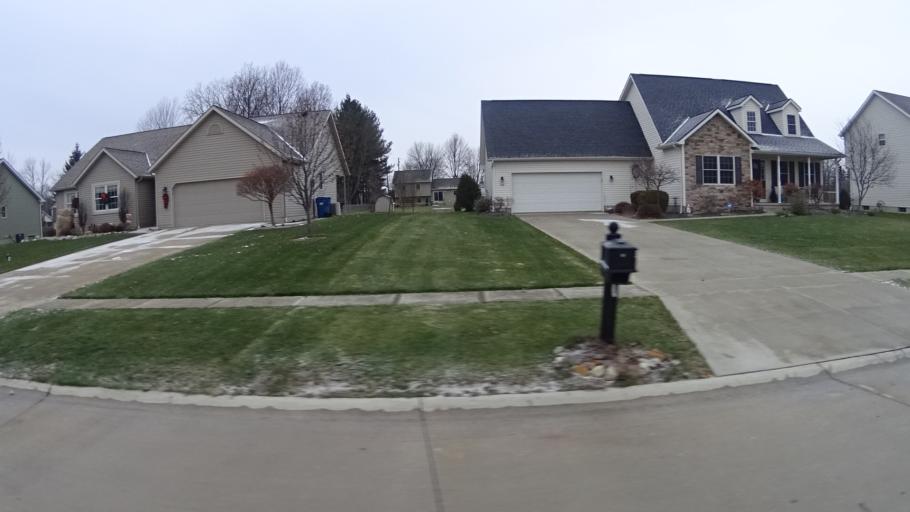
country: US
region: Ohio
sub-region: Lorain County
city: Grafton
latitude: 41.2838
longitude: -82.0495
